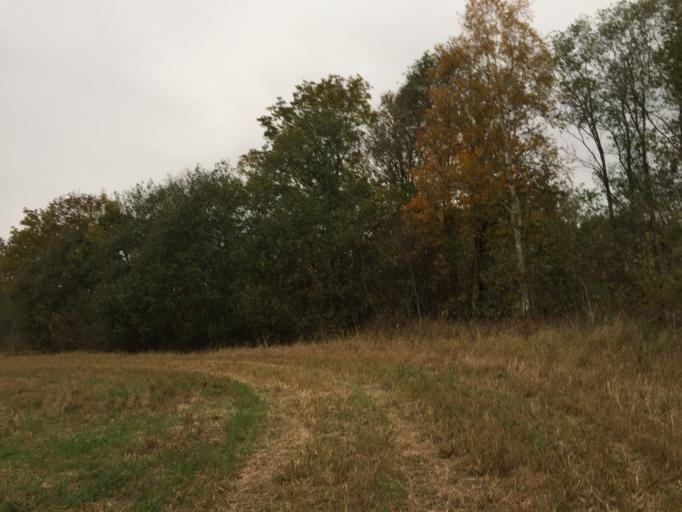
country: LV
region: Dobeles Rajons
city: Dobele
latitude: 56.6783
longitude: 23.4369
